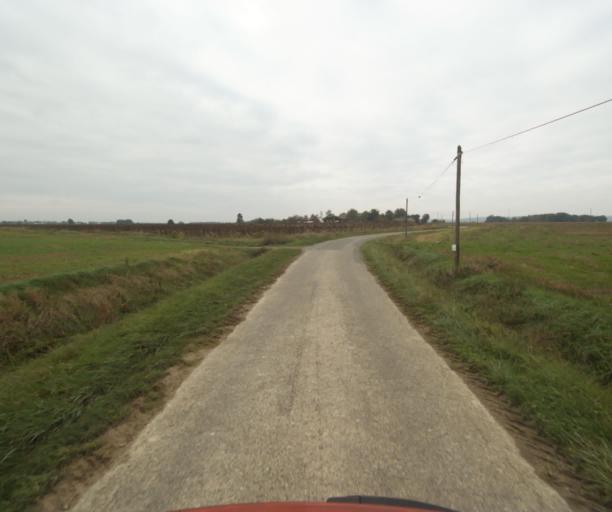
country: FR
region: Midi-Pyrenees
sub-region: Departement du Tarn-et-Garonne
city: Verdun-sur-Garonne
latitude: 43.8102
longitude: 1.1896
